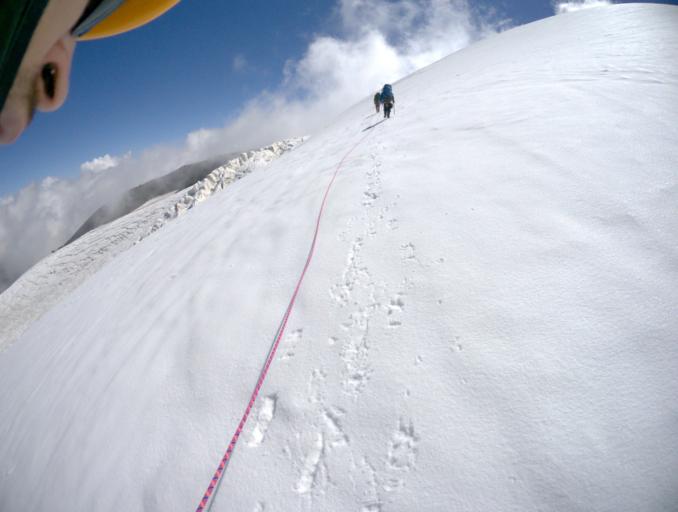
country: RU
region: Kabardino-Balkariya
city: Terskol
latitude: 43.3821
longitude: 42.4423
